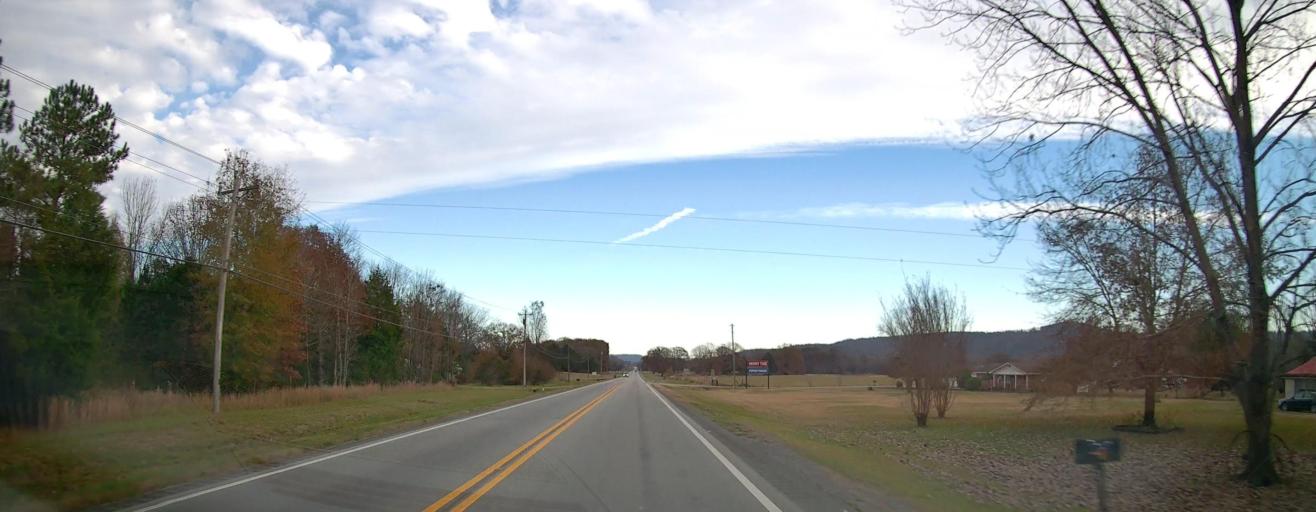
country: US
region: Alabama
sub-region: Morgan County
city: Falkville
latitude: 34.4310
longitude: -86.7313
